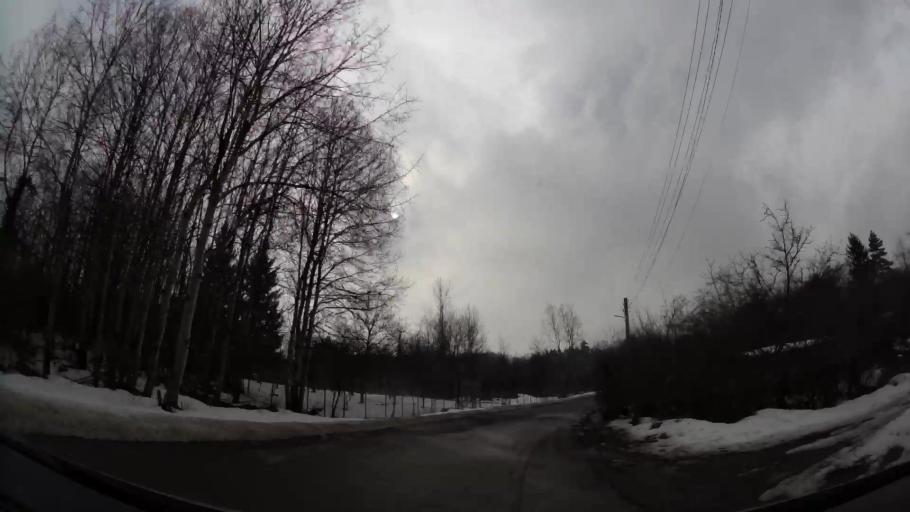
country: BG
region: Sofiya
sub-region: Obshtina Bozhurishte
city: Bozhurishte
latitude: 42.6535
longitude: 23.2003
